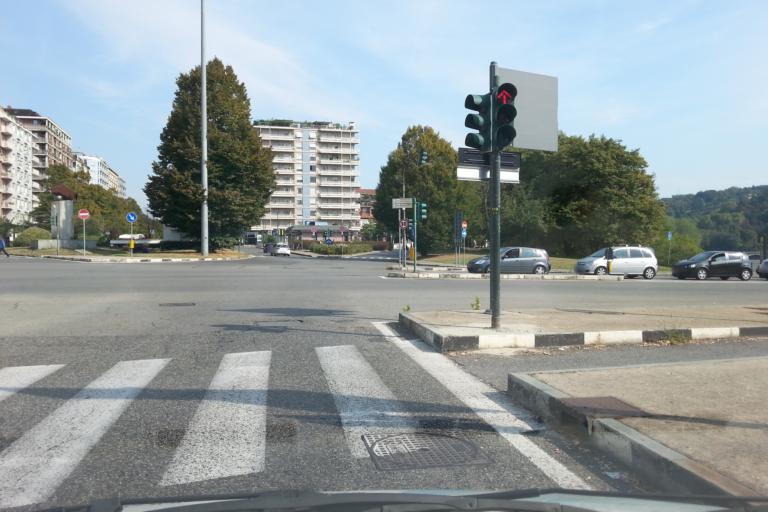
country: IT
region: Piedmont
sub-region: Provincia di Torino
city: Turin
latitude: 45.0414
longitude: 7.6768
